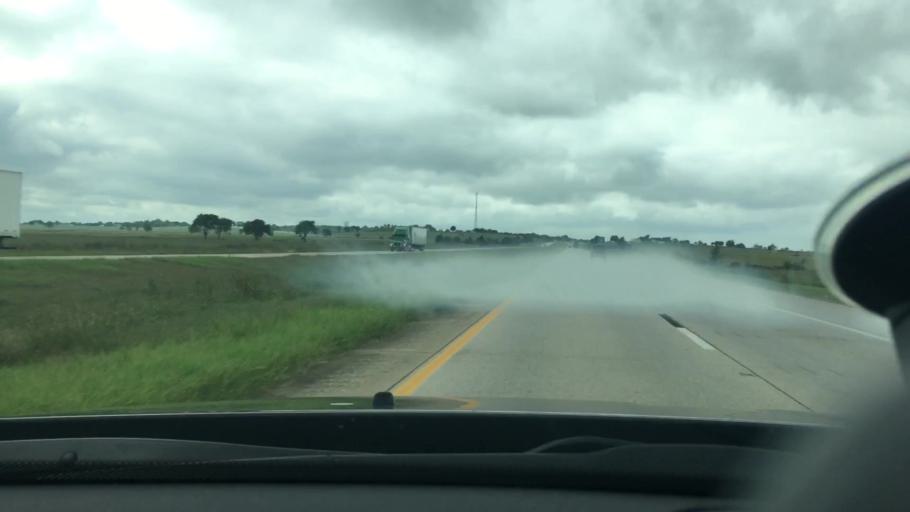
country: US
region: Oklahoma
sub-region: Bryan County
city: Durant
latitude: 34.1532
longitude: -96.2617
